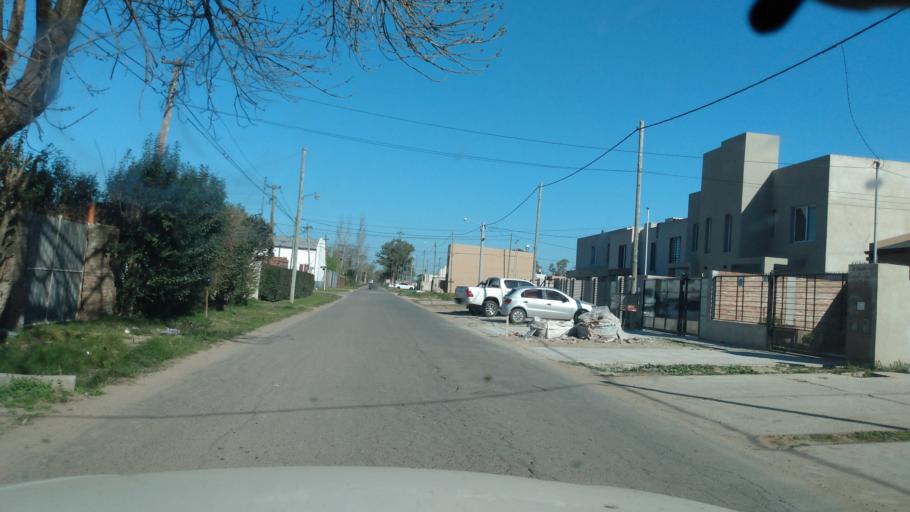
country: AR
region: Buenos Aires
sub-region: Partido de Lujan
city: Lujan
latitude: -34.5782
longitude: -59.0981
